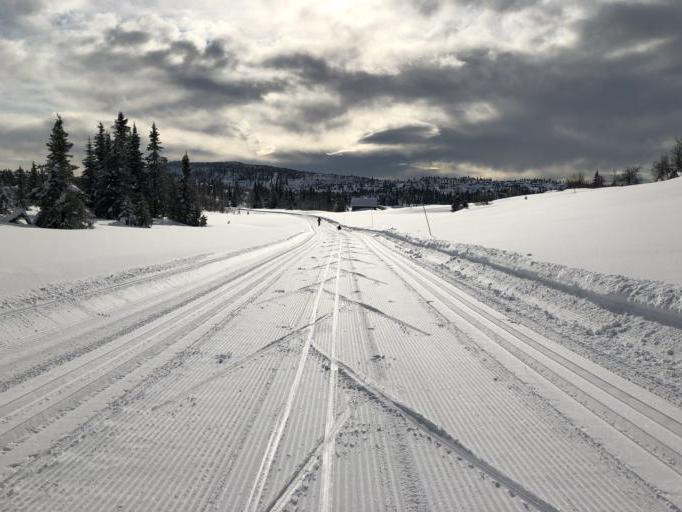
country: NO
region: Oppland
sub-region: Gausdal
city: Segalstad bru
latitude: 61.3178
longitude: 10.0594
